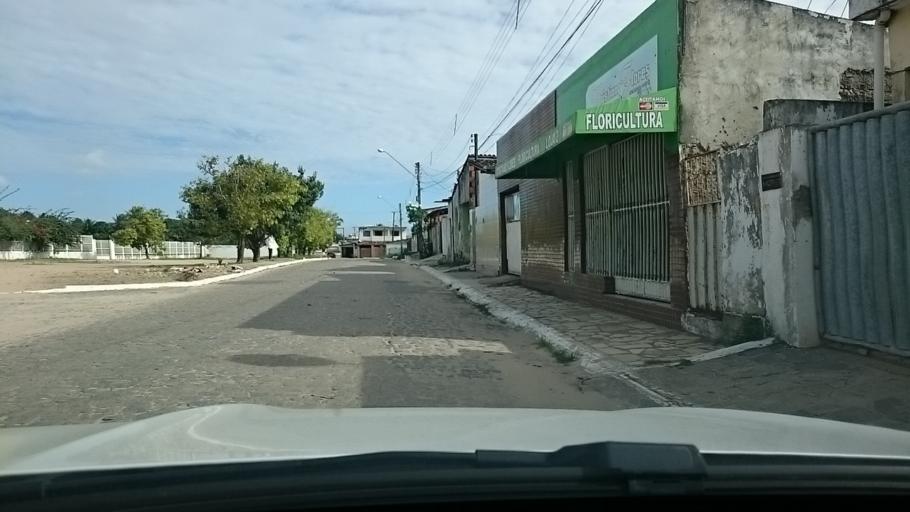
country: BR
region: Paraiba
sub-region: Joao Pessoa
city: Joao Pessoa
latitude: -7.1714
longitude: -34.8540
